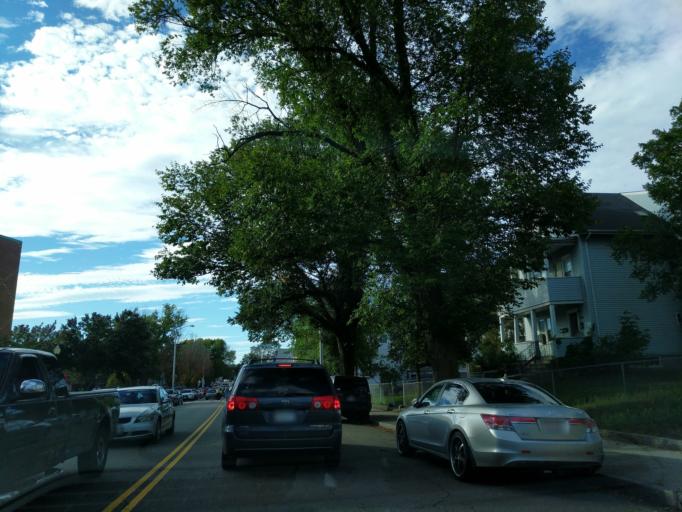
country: US
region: Massachusetts
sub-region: Middlesex County
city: Malden
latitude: 42.4221
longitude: -71.0594
